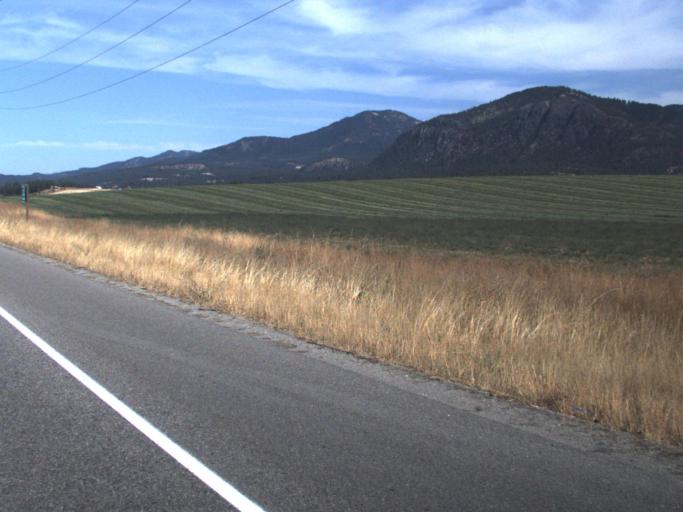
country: US
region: Washington
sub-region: Stevens County
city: Chewelah
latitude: 48.2303
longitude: -117.7153
